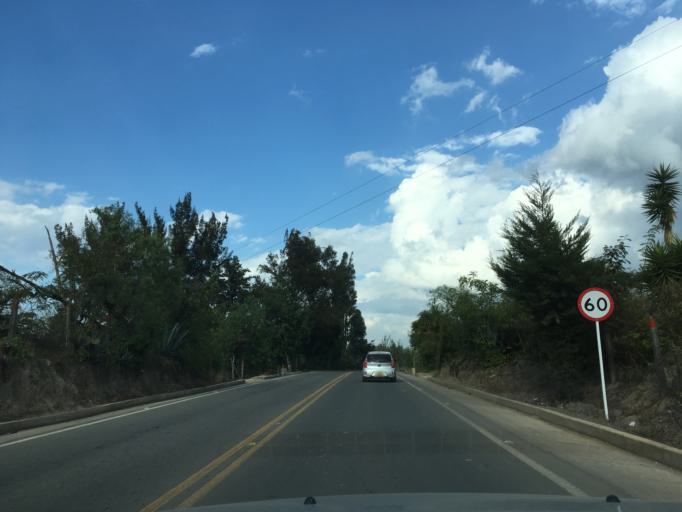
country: CO
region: Boyaca
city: Sutamarchan
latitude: 5.6187
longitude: -73.6113
